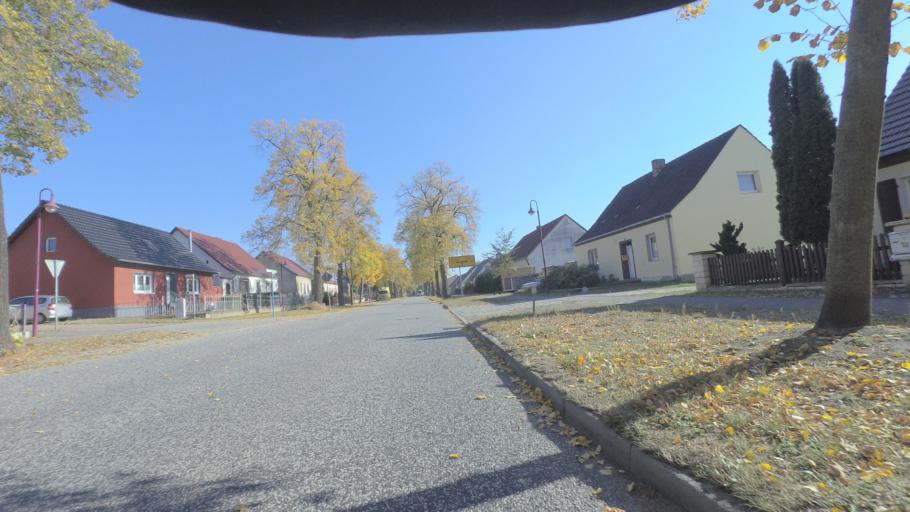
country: DE
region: Brandenburg
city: Mittenwalde
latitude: 52.2454
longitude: 13.4928
